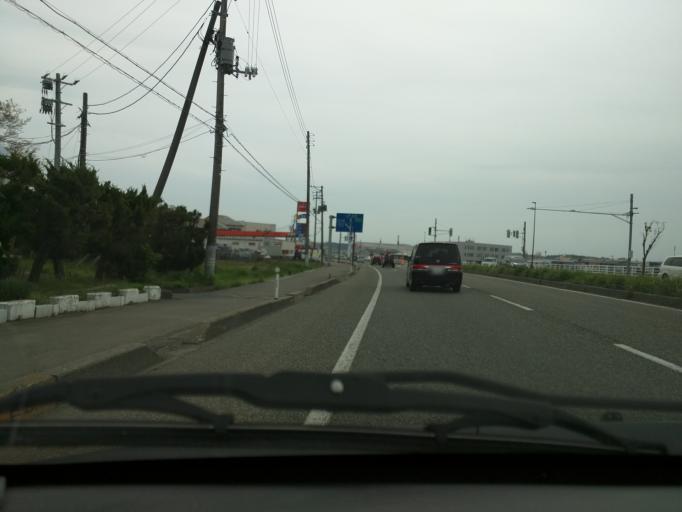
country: JP
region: Niigata
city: Nagaoka
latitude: 37.4546
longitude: 138.8048
